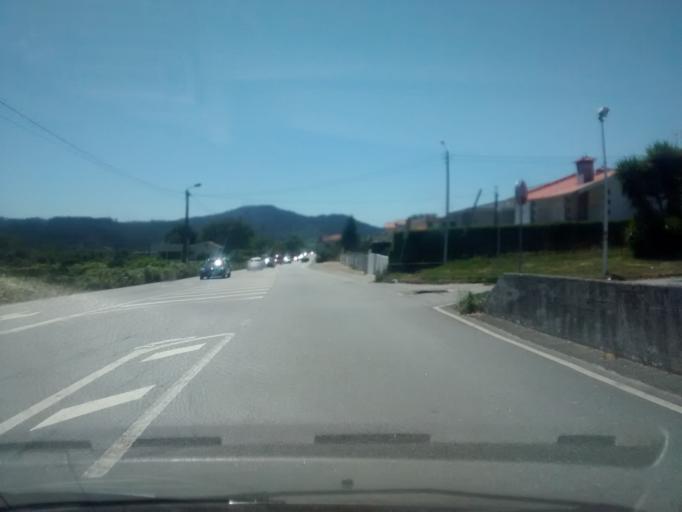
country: PT
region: Braga
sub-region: Braga
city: Braga
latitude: 41.5339
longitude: -8.4612
